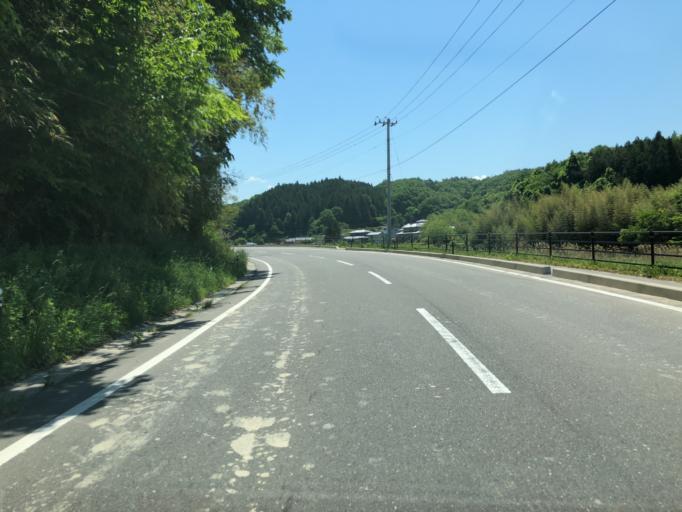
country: JP
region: Fukushima
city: Miharu
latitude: 37.5012
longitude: 140.4760
